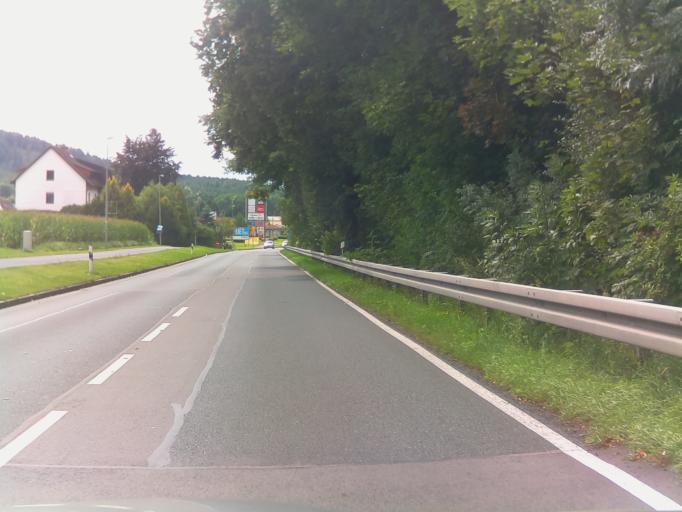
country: DE
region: Bavaria
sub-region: Upper Franconia
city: Ebersdorf
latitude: 50.3397
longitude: 11.1427
